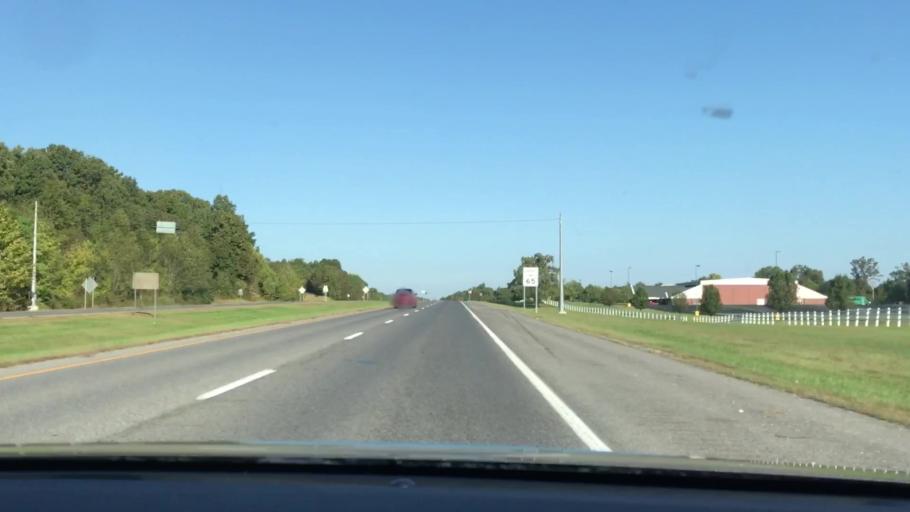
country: US
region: Kentucky
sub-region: Marshall County
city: Benton
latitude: 36.7670
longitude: -88.3121
